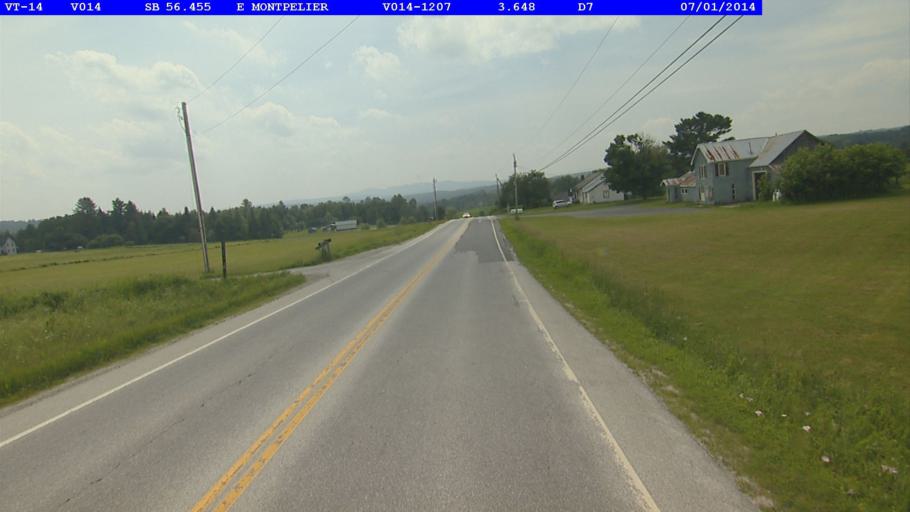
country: US
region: Vermont
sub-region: Washington County
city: Barre
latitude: 44.2830
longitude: -72.4697
